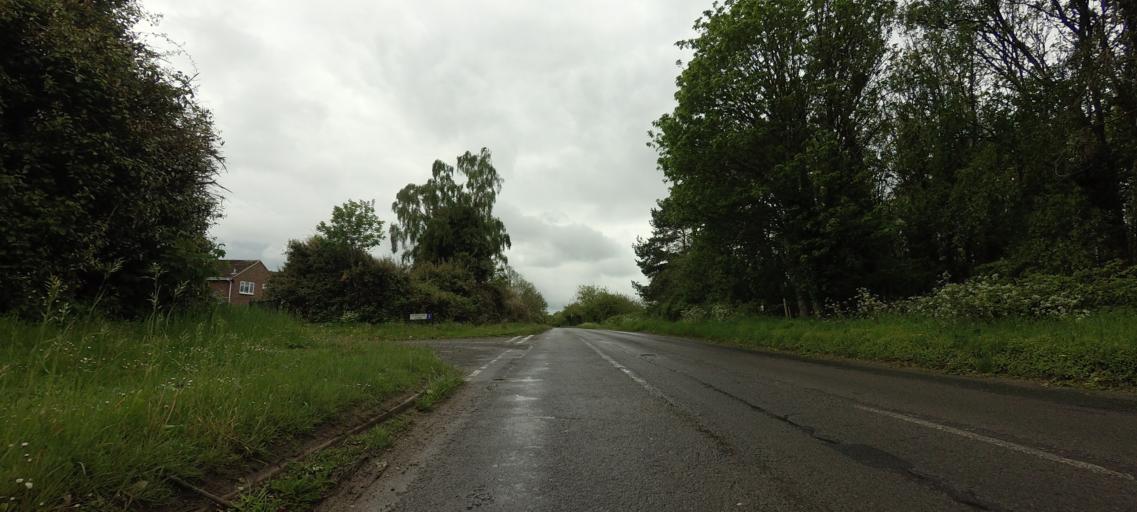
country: GB
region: England
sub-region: Dorset
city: Bovington Camp
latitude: 50.6953
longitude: -2.3338
